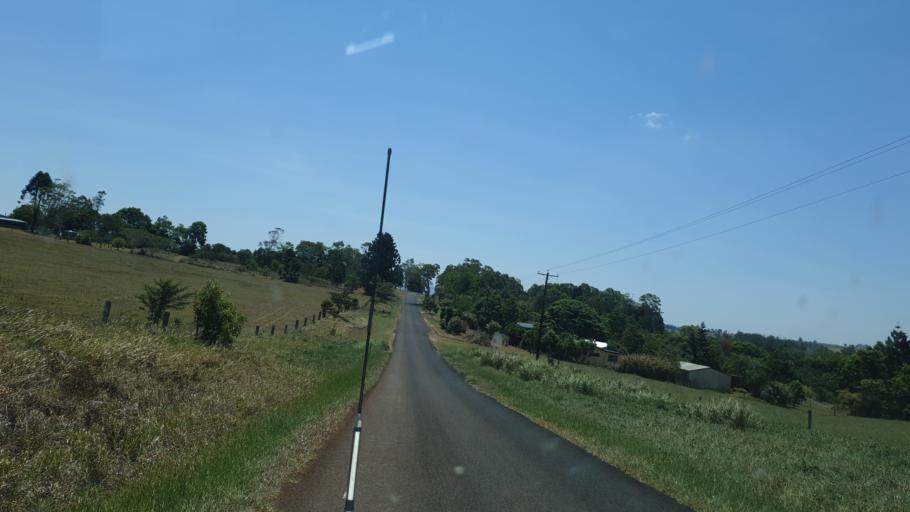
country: AU
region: Queensland
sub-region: Tablelands
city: Atherton
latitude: -17.3499
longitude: 145.6196
